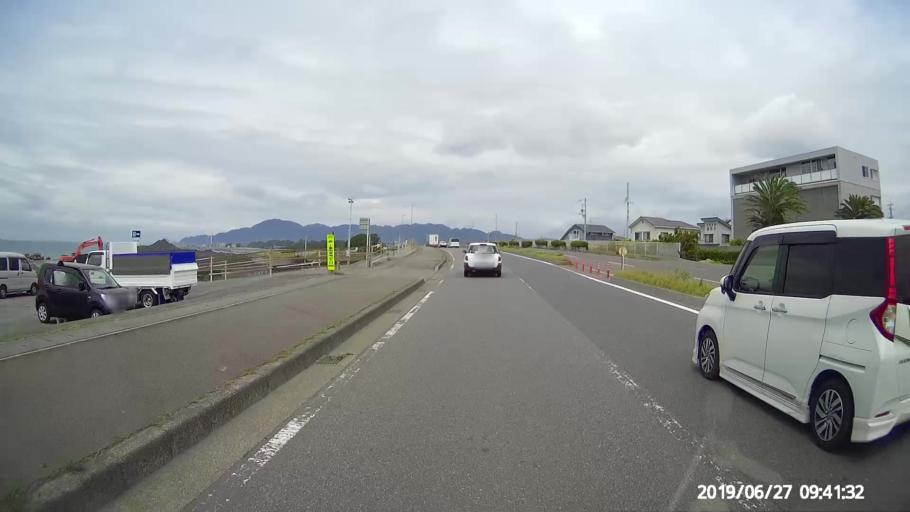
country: JP
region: Shizuoka
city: Shizuoka-shi
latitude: 34.9446
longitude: 138.4199
